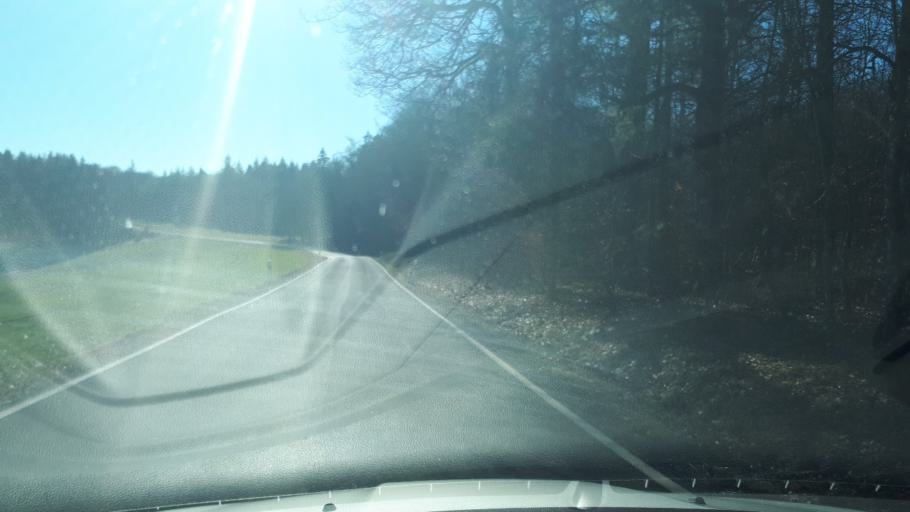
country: DE
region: Rheinland-Pfalz
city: Ellscheid
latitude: 50.1659
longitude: 6.9145
